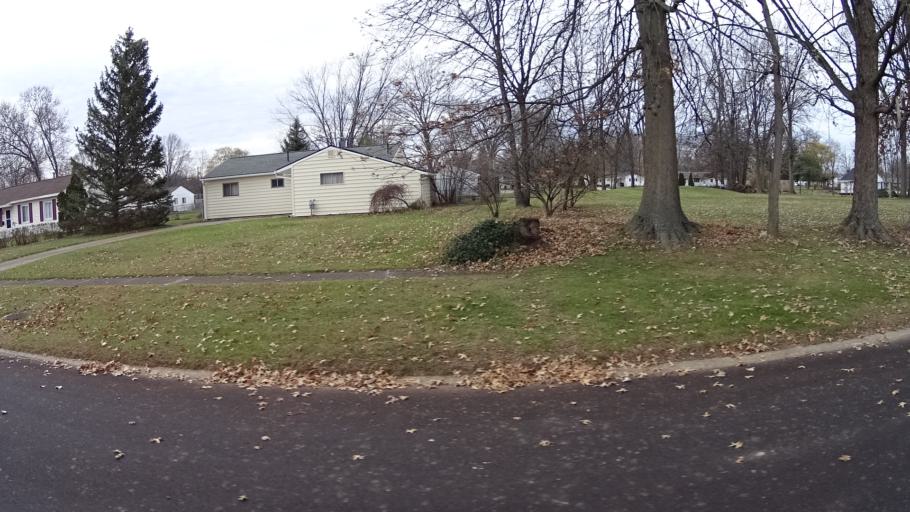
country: US
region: Ohio
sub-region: Lorain County
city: North Ridgeville
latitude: 41.3840
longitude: -81.9965
